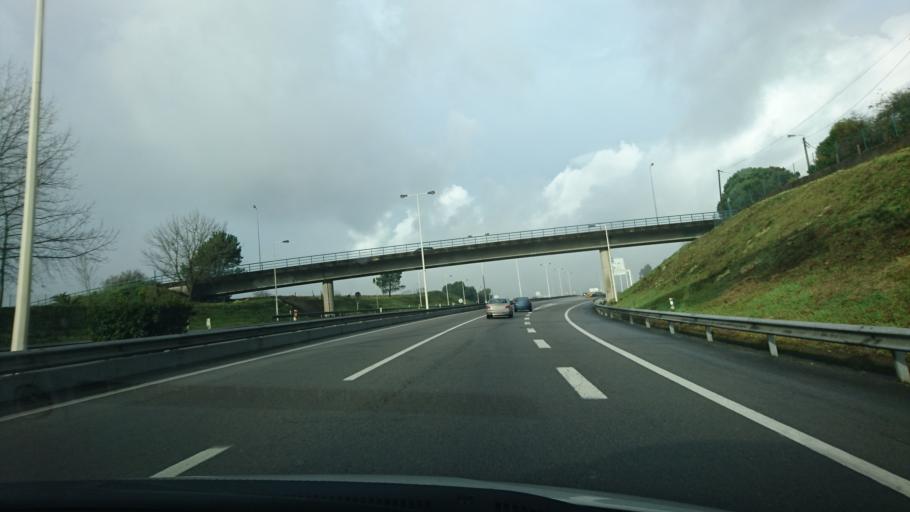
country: PT
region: Porto
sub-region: Gondomar
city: Valbom
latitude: 41.1560
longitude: -8.5581
